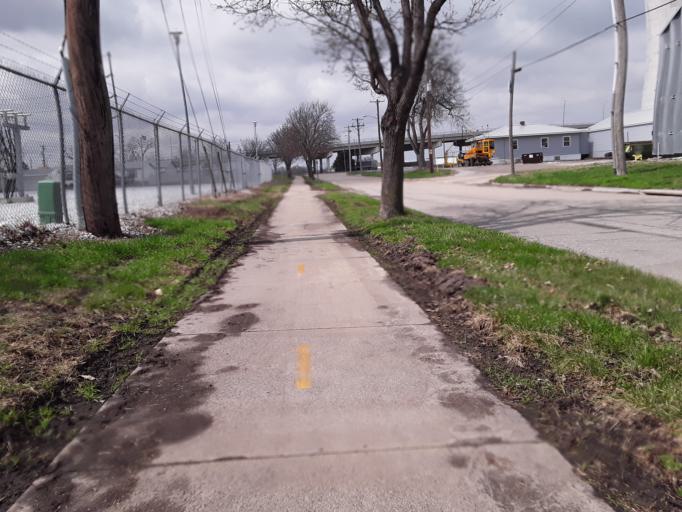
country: US
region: Nebraska
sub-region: Lancaster County
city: Lincoln
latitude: 40.8352
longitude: -96.6798
